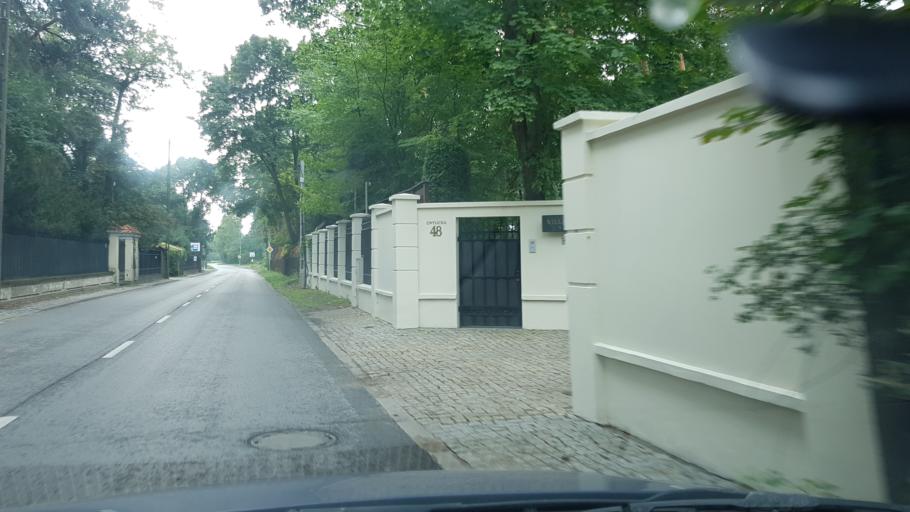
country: PL
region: Masovian Voivodeship
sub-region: Powiat piaseczynski
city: Konstancin-Jeziorna
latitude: 52.0723
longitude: 21.0991
